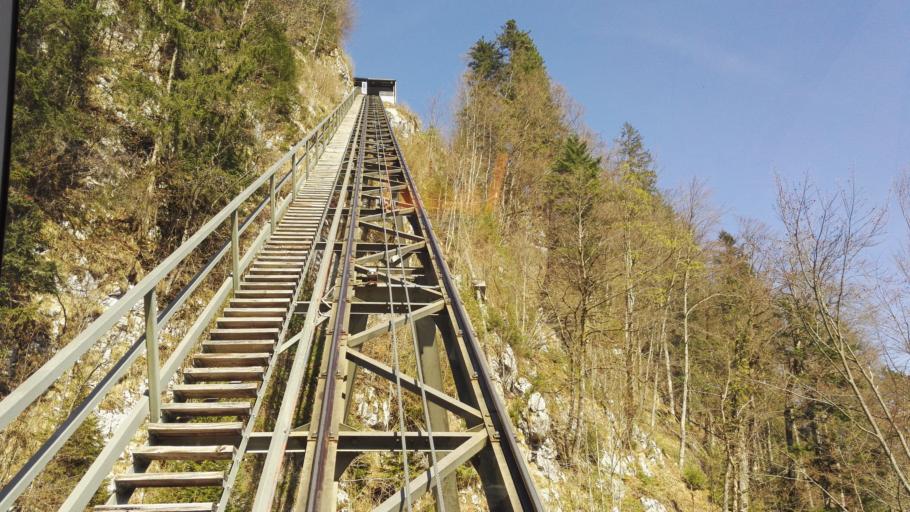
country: AT
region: Upper Austria
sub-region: Politischer Bezirk Gmunden
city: Bad Goisern
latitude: 47.5591
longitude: 13.6444
